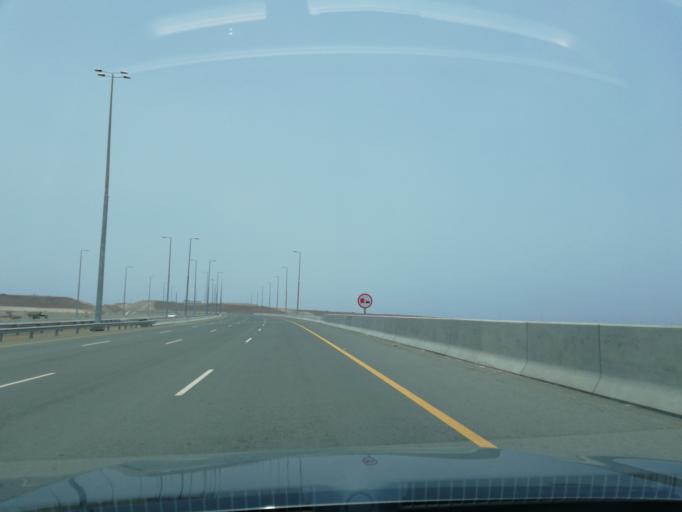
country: OM
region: Al Batinah
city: Al Liwa'
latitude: 24.5340
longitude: 56.5004
